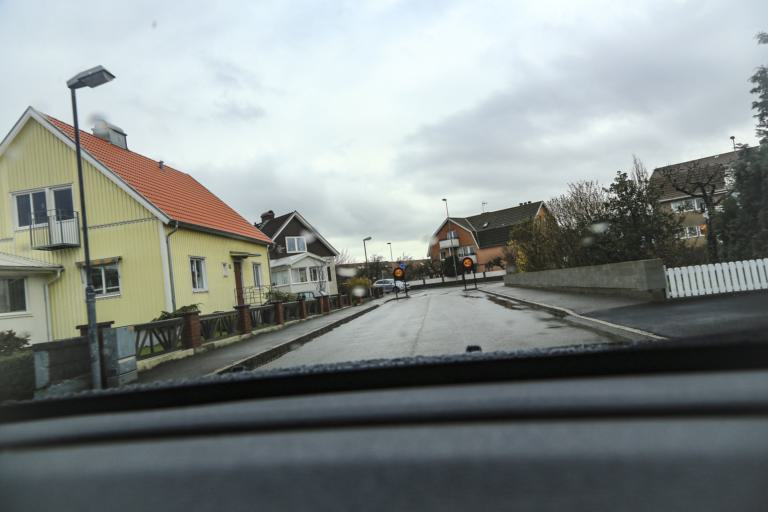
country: SE
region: Halland
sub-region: Varbergs Kommun
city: Varberg
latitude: 57.1070
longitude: 12.2661
